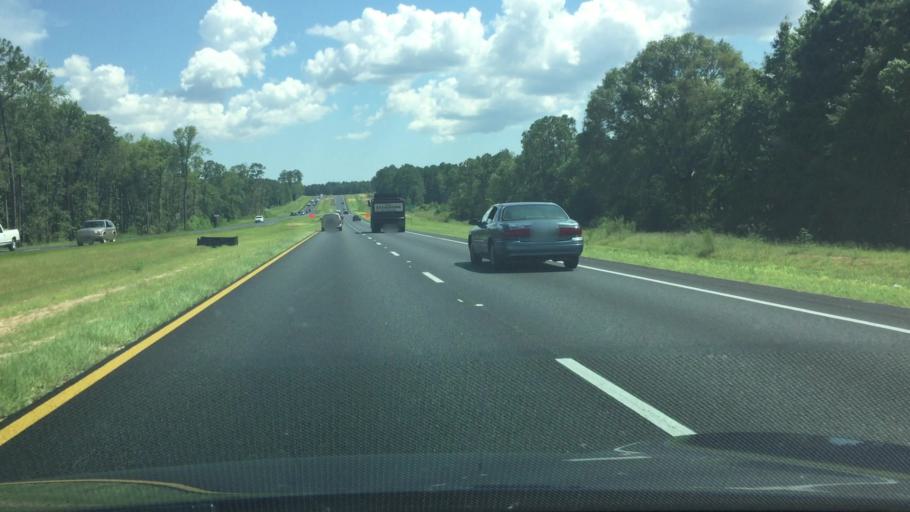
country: US
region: Florida
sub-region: Walton County
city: DeFuniak Springs
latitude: 30.6793
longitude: -86.1225
